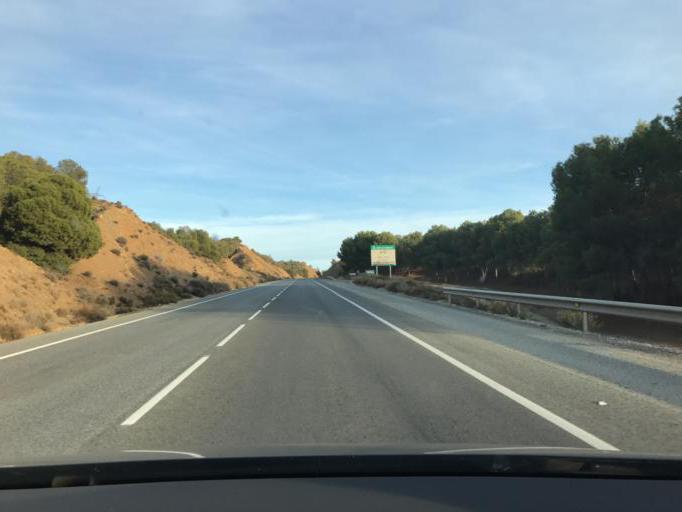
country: ES
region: Andalusia
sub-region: Provincia de Granada
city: Guadix
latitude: 37.2713
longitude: -3.1030
